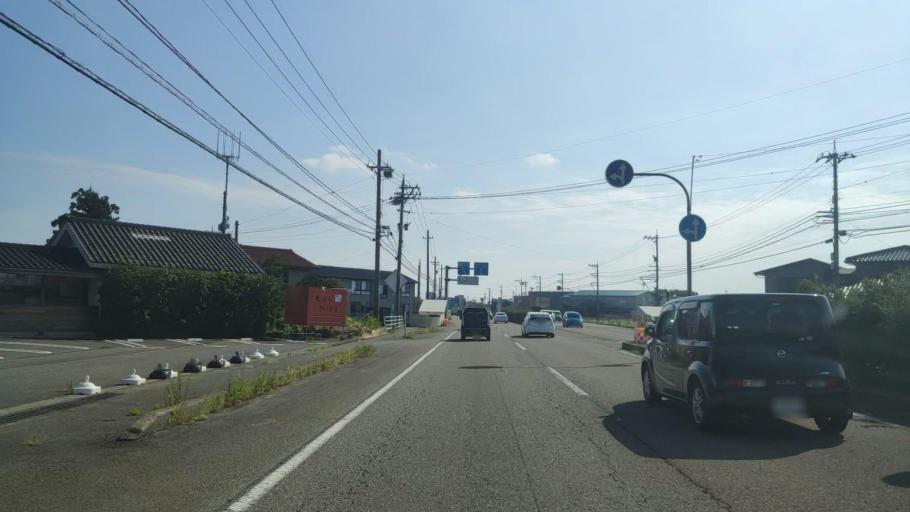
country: JP
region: Ishikawa
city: Matsuto
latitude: 36.5051
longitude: 136.5512
